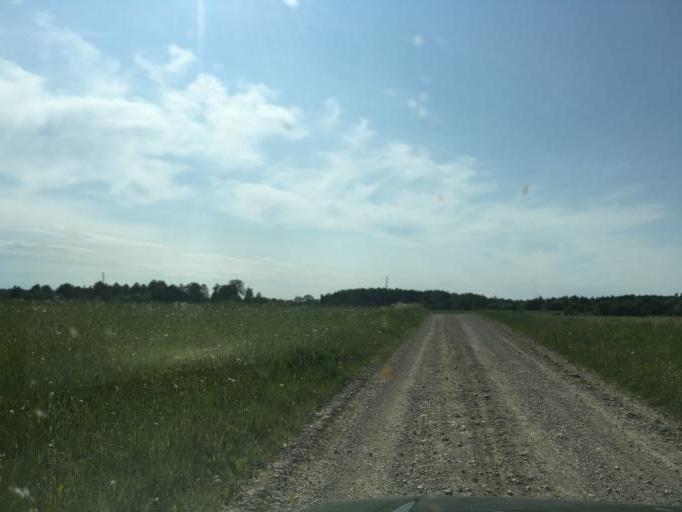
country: LV
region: Dundaga
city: Dundaga
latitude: 57.5521
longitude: 22.4644
